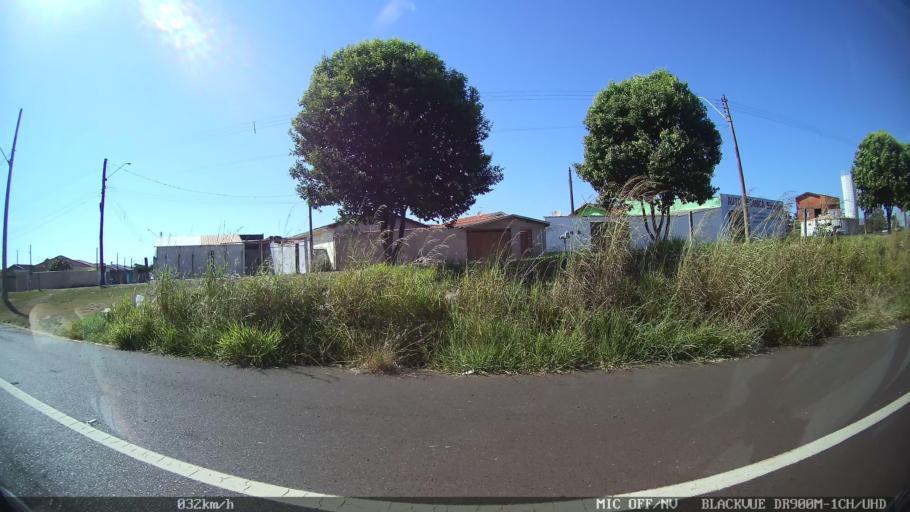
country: BR
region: Sao Paulo
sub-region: Batatais
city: Batatais
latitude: -20.9151
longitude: -47.5834
